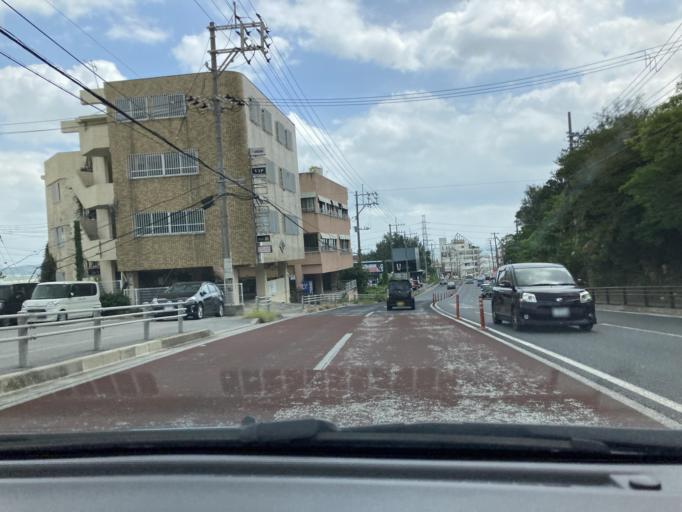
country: JP
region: Okinawa
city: Okinawa
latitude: 26.3331
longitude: 127.8205
